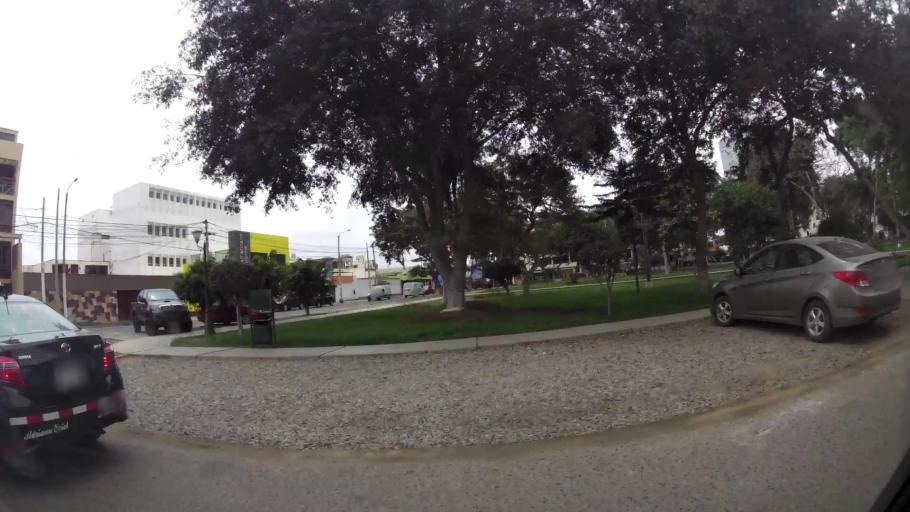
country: PE
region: La Libertad
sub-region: Provincia de Trujillo
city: Buenos Aires
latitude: -8.1318
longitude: -79.0405
